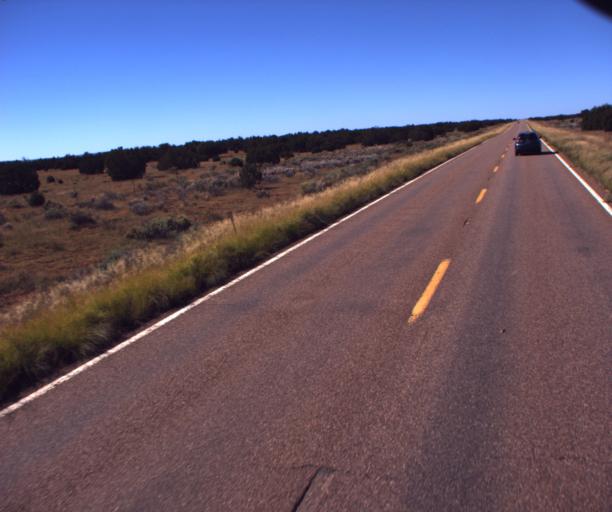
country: US
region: Arizona
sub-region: Navajo County
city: Heber-Overgaard
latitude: 34.4712
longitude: -110.3613
